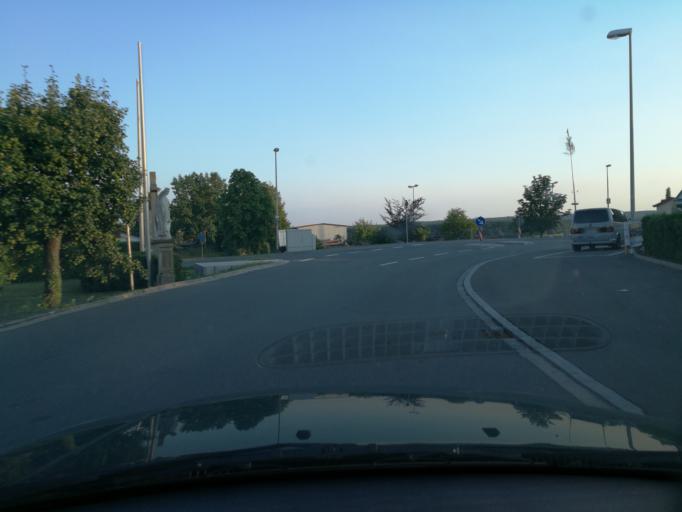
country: DE
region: Bavaria
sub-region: Regierungsbezirk Mittelfranken
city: Hessdorf
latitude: 49.6369
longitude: 10.9028
